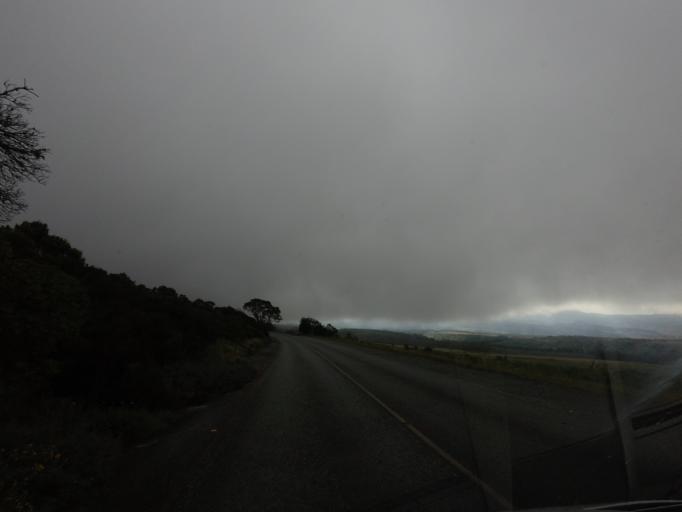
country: ZA
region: Mpumalanga
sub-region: Ehlanzeni District
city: Graksop
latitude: -24.8699
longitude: 30.8935
